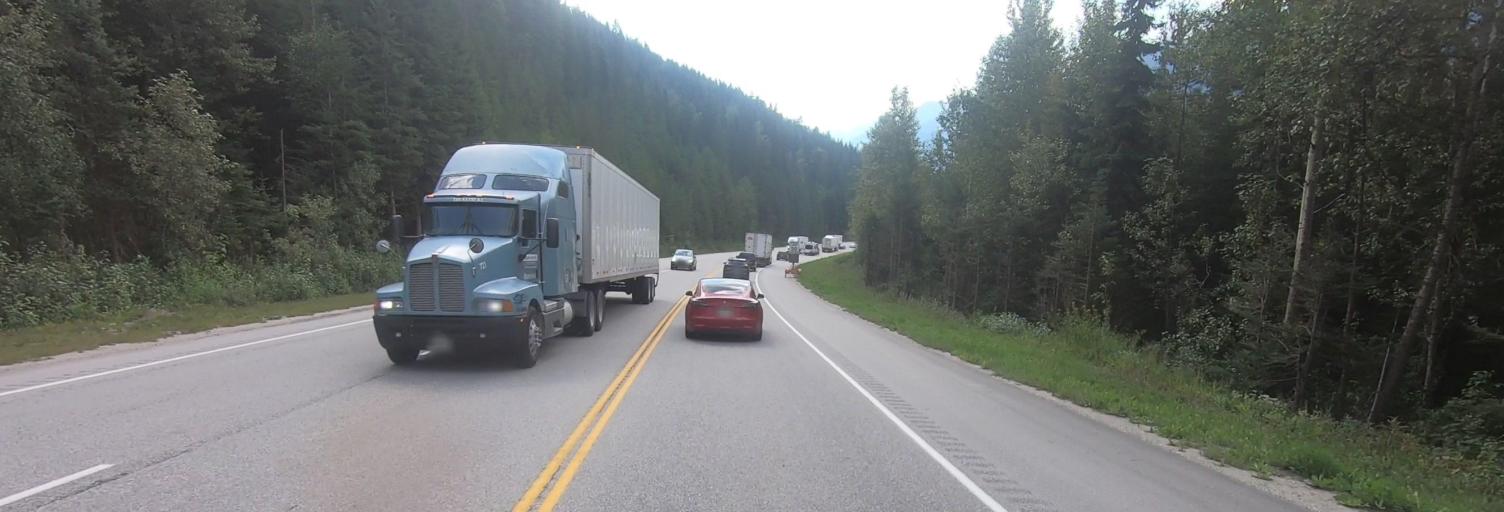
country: CA
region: British Columbia
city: Golden
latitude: 51.4411
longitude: -117.4771
